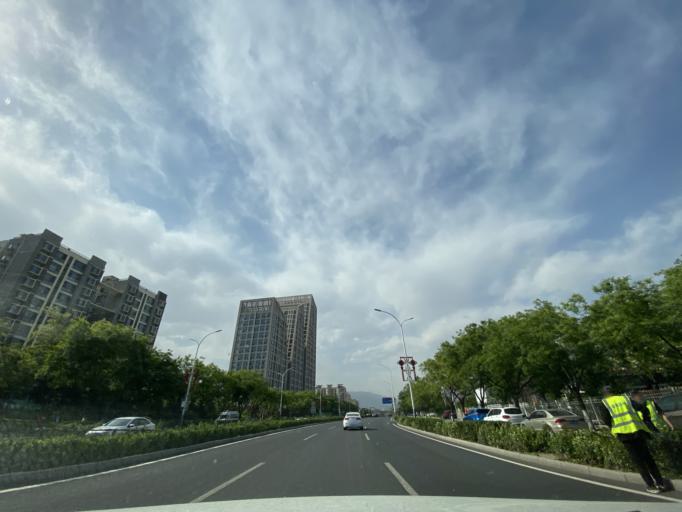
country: CN
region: Beijing
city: Dayu
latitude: 39.9407
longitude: 116.1019
